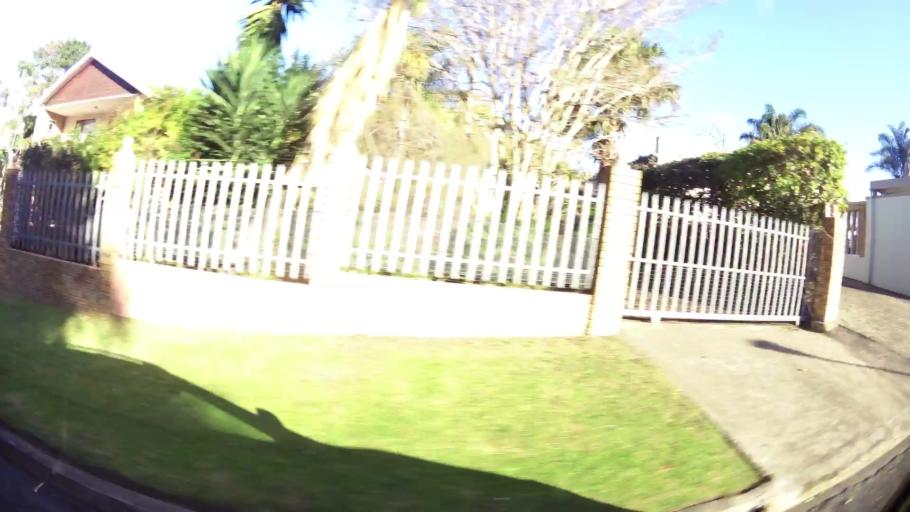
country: ZA
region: Western Cape
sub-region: Eden District Municipality
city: George
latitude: -33.9498
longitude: 22.4536
